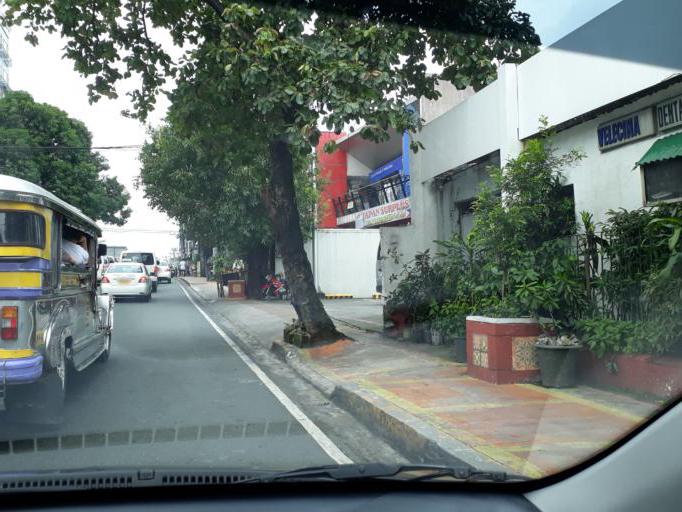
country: PH
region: Metro Manila
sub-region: Quezon City
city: Quezon City
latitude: 14.6301
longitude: 121.0441
